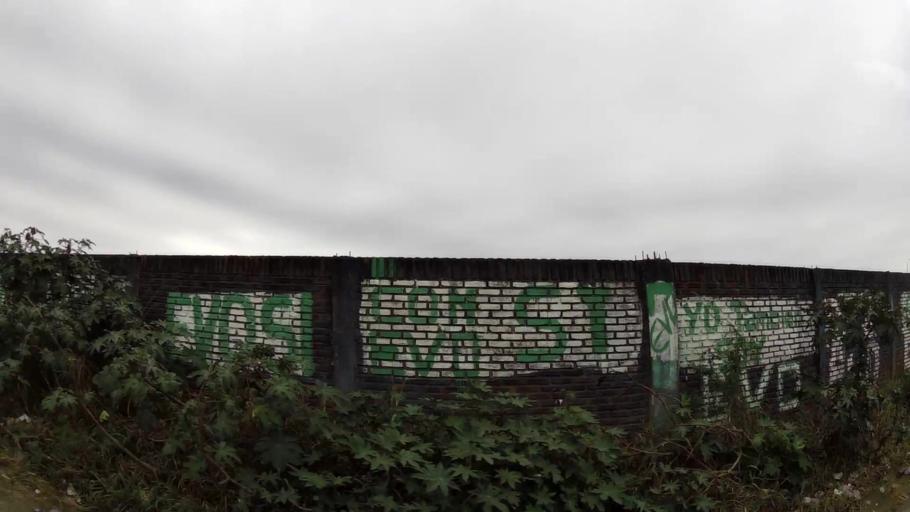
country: BO
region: Santa Cruz
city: Santa Cruz de la Sierra
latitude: -17.8218
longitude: -63.1629
